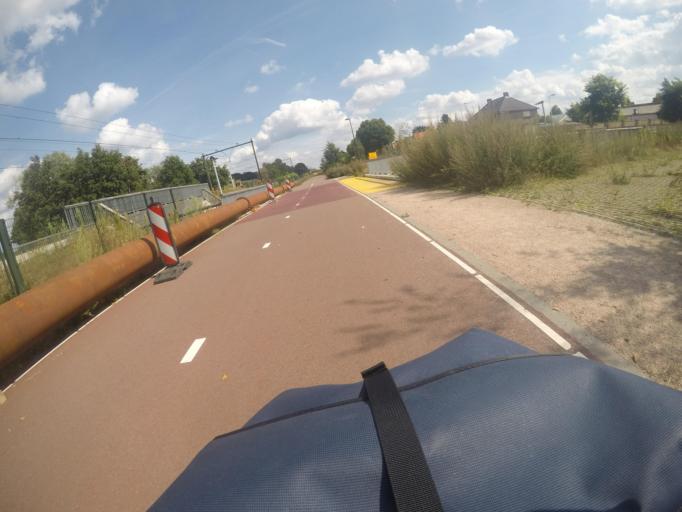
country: NL
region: Gelderland
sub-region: Gemeente Ede
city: Ede
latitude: 52.0304
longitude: 5.6574
